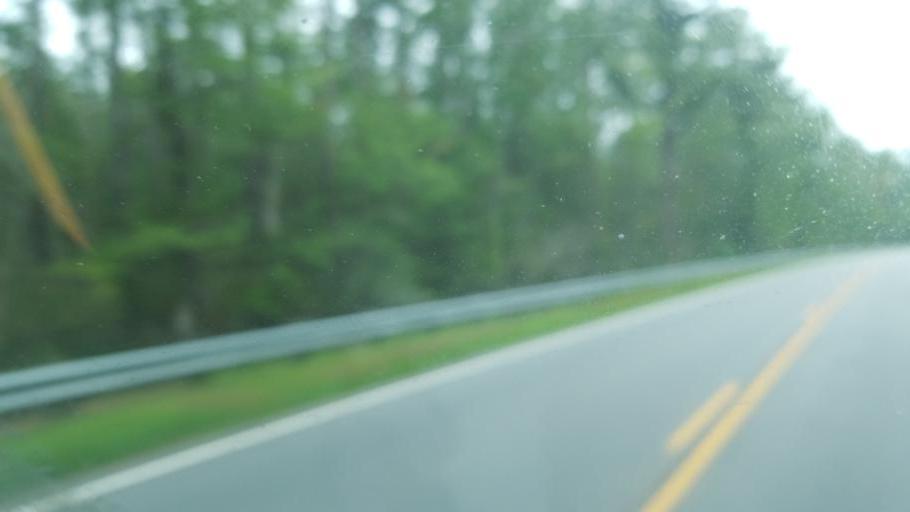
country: US
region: North Carolina
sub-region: Dare County
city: Manteo
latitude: 35.8815
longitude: -75.9475
